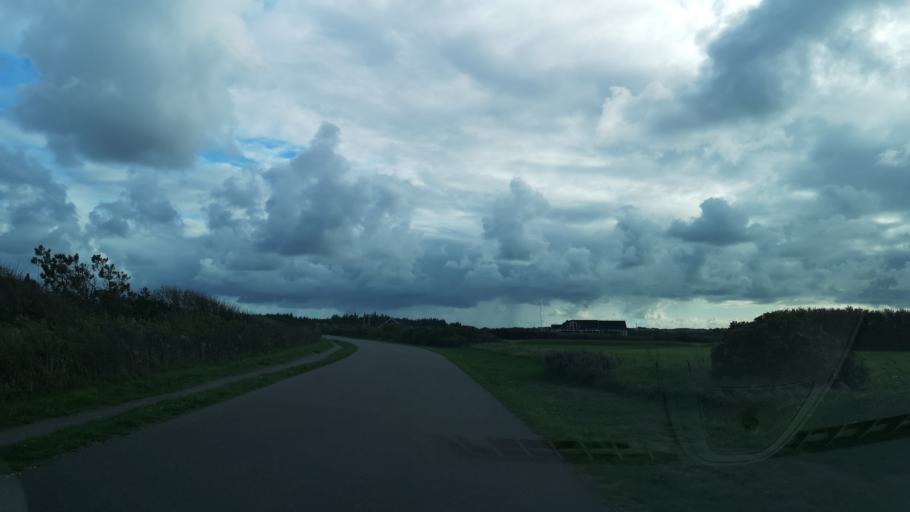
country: DK
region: Central Jutland
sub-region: Ringkobing-Skjern Kommune
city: Ringkobing
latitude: 56.1329
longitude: 8.1320
